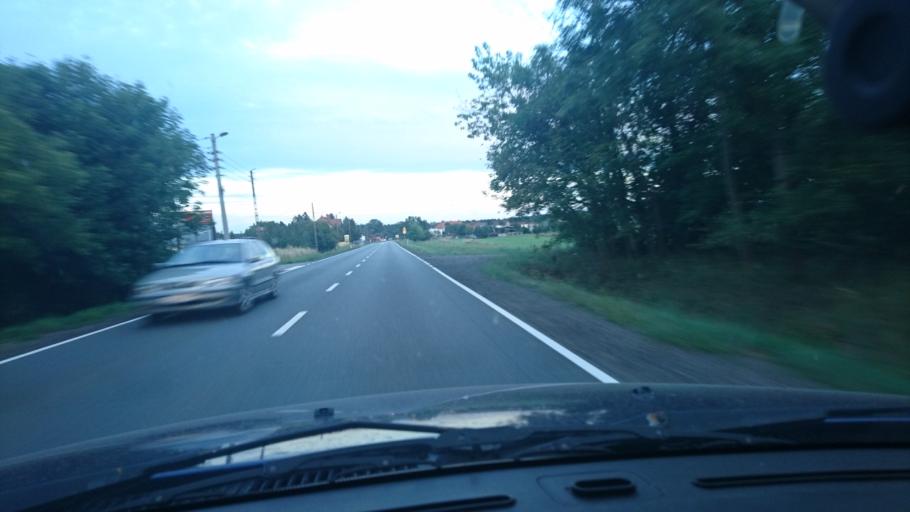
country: PL
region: Silesian Voivodeship
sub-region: Powiat tarnogorski
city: Tworog
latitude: 50.5075
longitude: 18.7615
